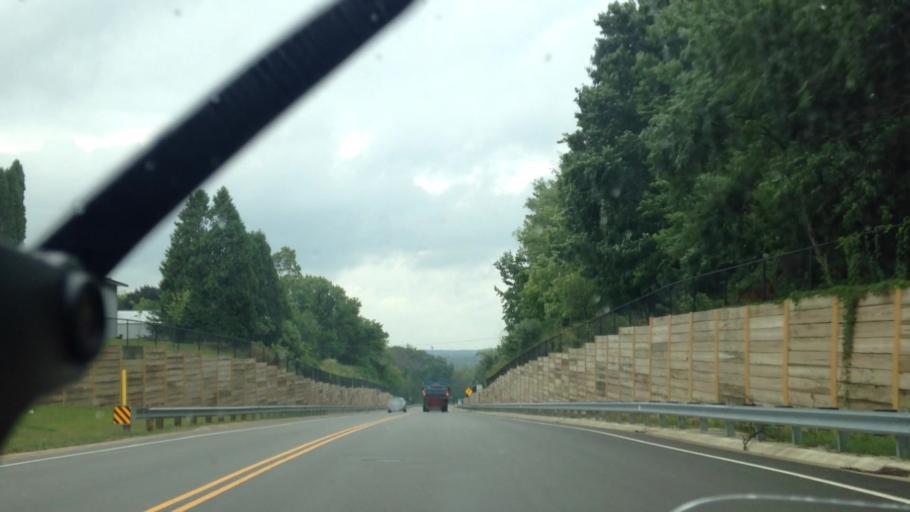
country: US
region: Wisconsin
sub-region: Washington County
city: Richfield
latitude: 43.2226
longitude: -88.1755
